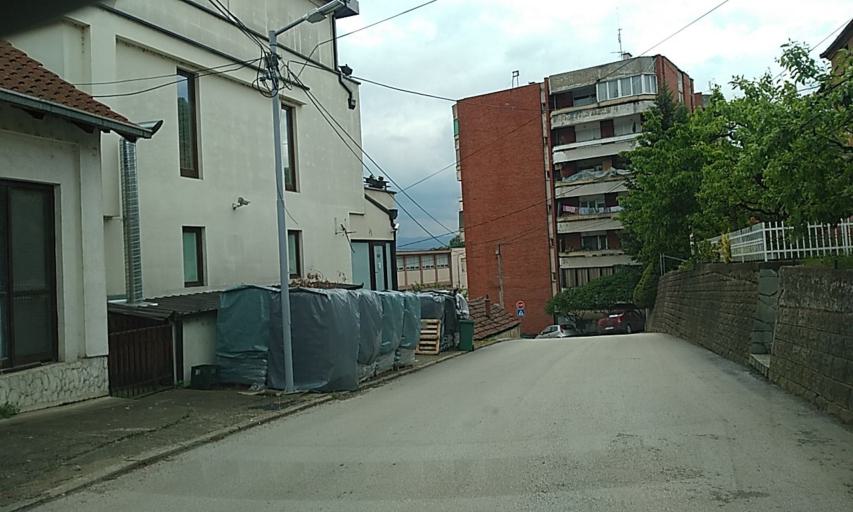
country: RS
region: Central Serbia
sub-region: Pcinjski Okrug
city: Vladicin Han
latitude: 42.7116
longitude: 22.0624
